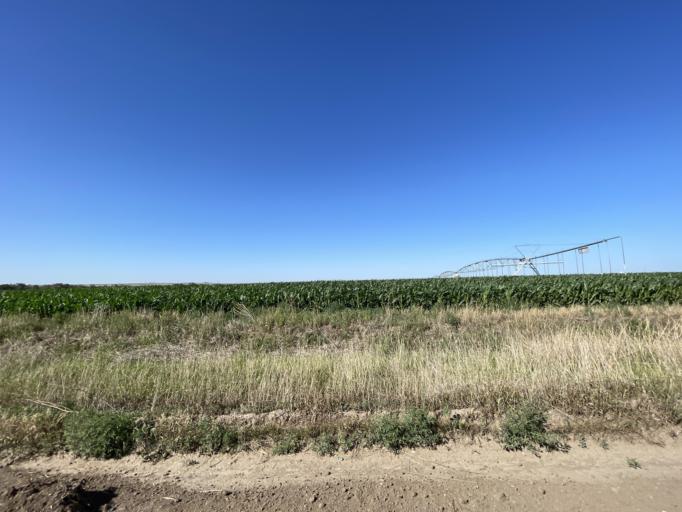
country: US
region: Nebraska
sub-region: Red Willow County
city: McCook
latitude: 40.2131
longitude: -100.6033
